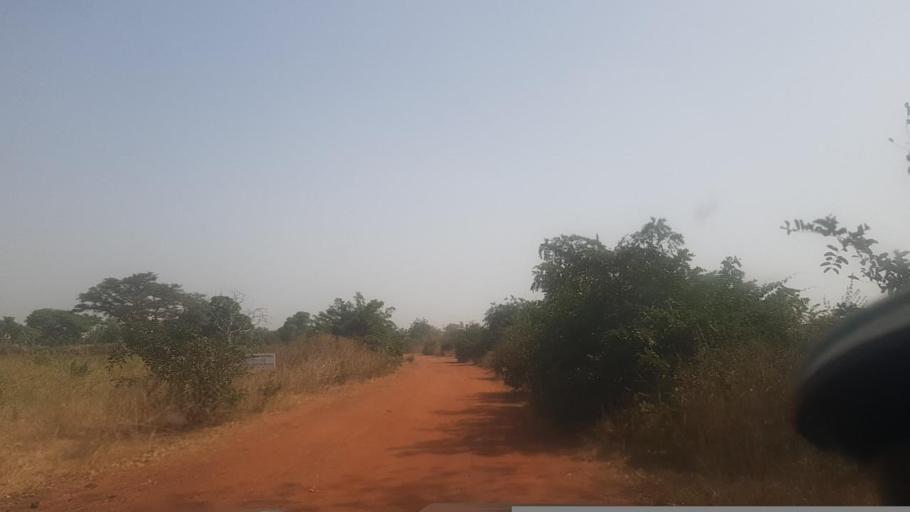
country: ML
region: Segou
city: Bla
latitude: 12.9147
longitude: -6.2500
